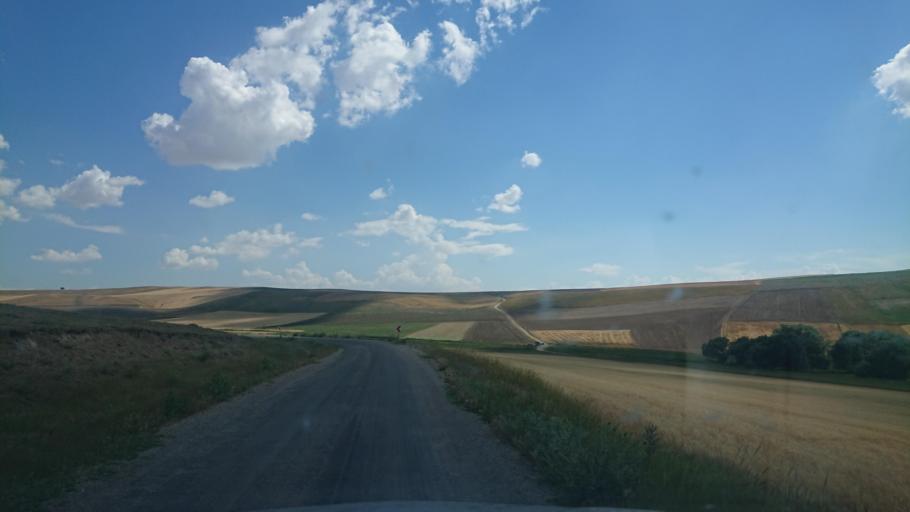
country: TR
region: Aksaray
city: Agacoren
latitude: 38.8235
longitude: 33.7903
